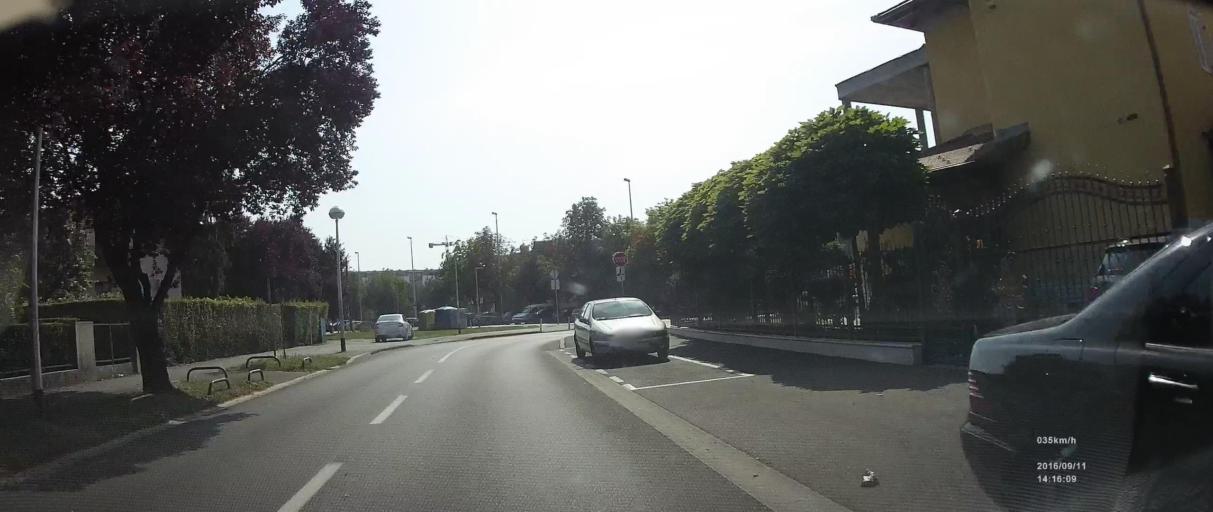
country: HR
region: Grad Zagreb
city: Zagreb
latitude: 45.8151
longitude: 16.0200
